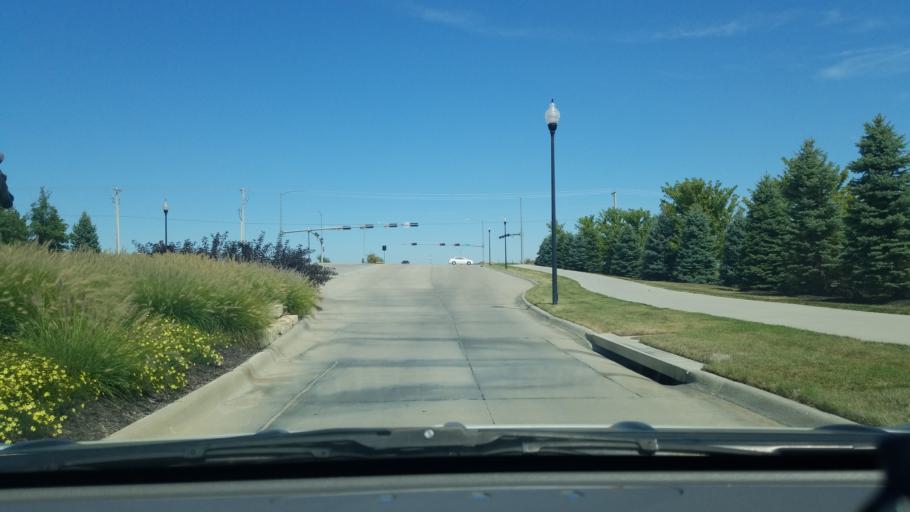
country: US
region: Nebraska
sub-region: Sarpy County
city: Papillion
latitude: 41.1465
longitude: -96.1010
